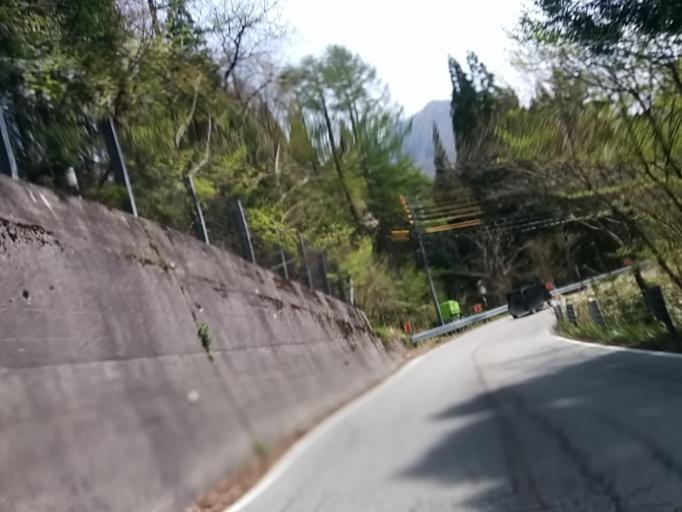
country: JP
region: Gifu
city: Takayama
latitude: 36.2227
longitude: 137.5414
